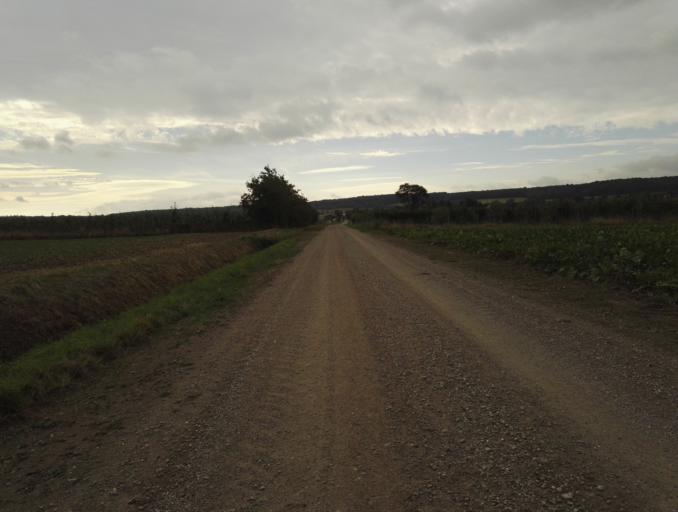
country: DE
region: Lower Saxony
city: Schellerten
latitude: 52.1422
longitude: 10.0642
